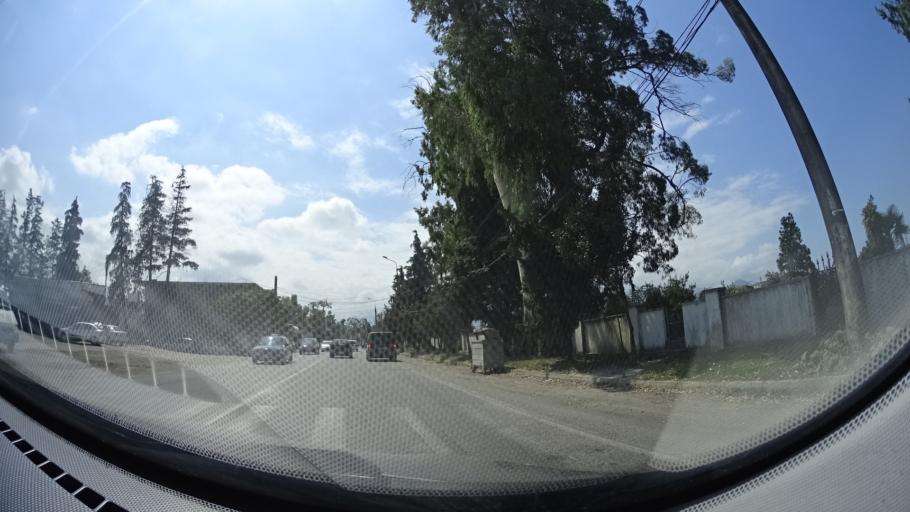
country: GE
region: Ajaria
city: Batumi
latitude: 41.6189
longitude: 41.6179
